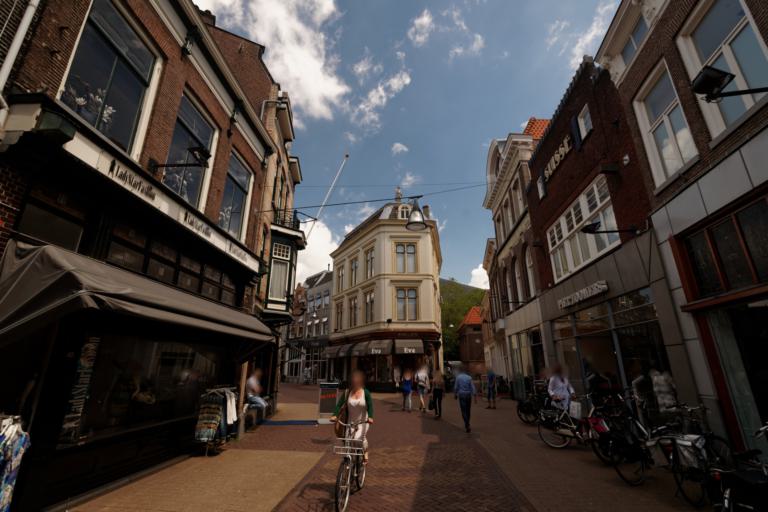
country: NL
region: Overijssel
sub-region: Gemeente Zwolle
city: Zwolle
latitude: 52.5111
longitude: 6.0909
